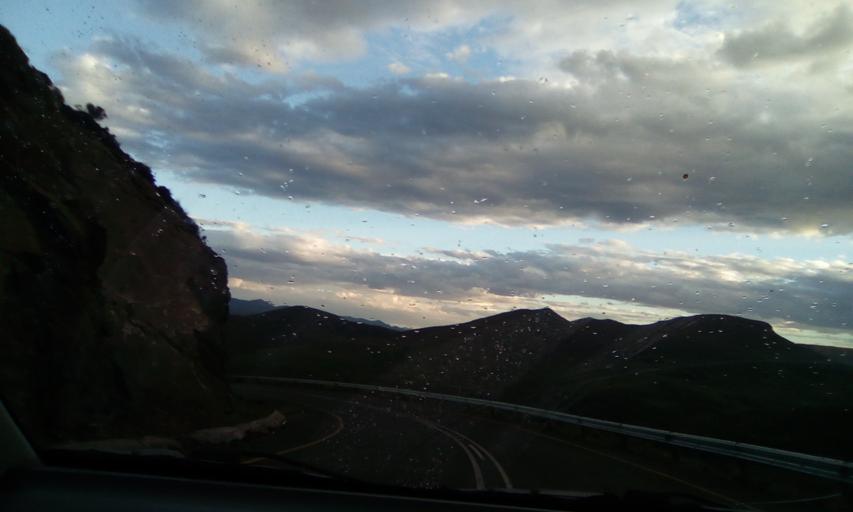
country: LS
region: Maseru
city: Nako
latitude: -29.7623
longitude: 27.9929
